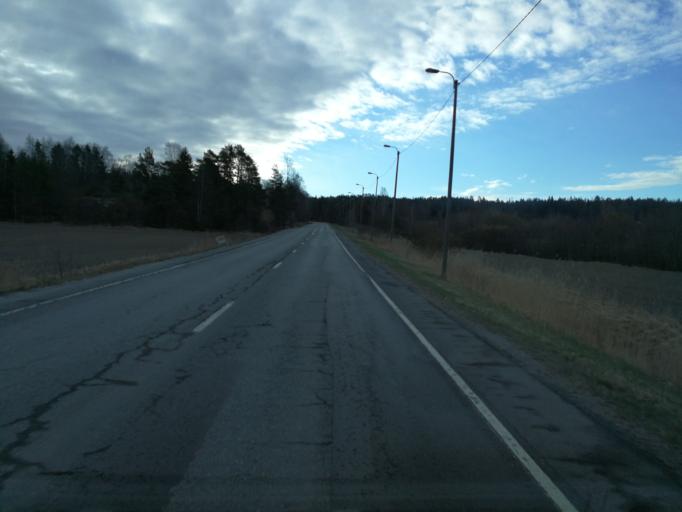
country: FI
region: Varsinais-Suomi
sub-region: Turku
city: Paimio
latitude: 60.4193
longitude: 22.6706
